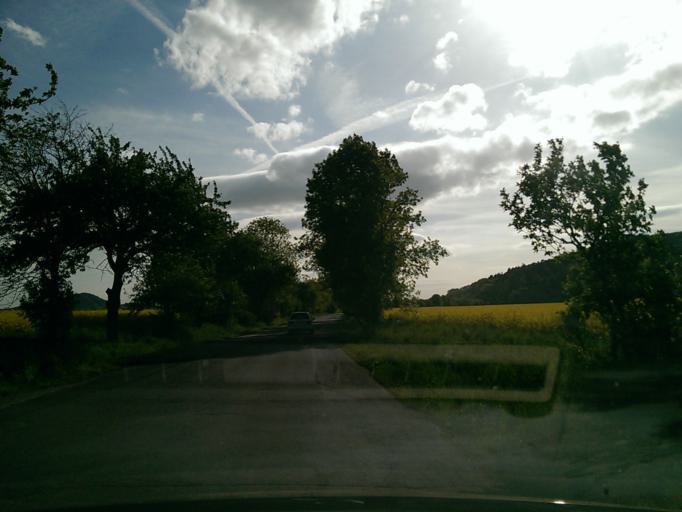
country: CZ
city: Doksy
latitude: 50.5597
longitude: 14.6443
